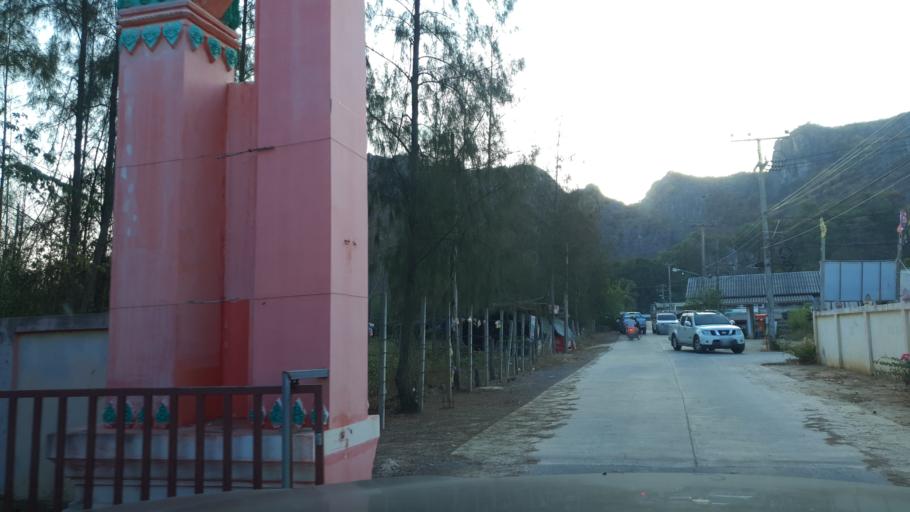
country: TH
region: Prachuap Khiri Khan
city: Sam Roi Yot
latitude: 12.2034
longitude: 100.0068
